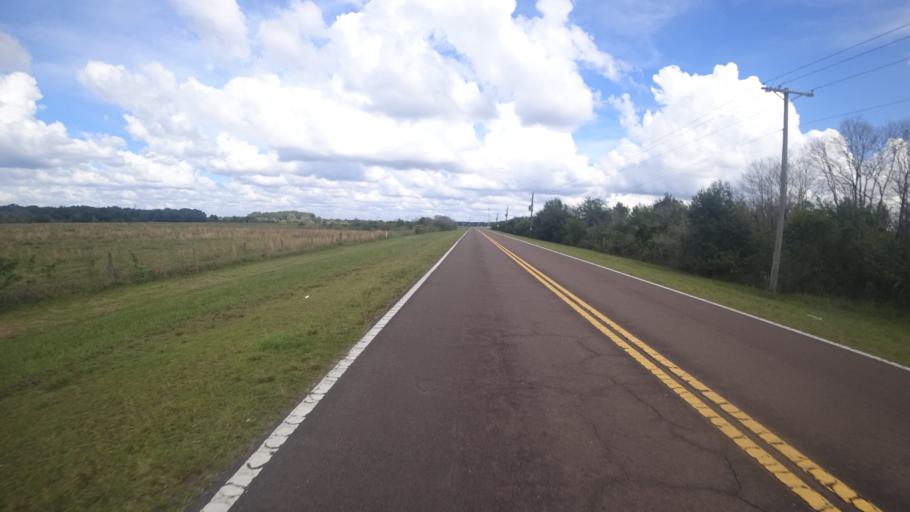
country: US
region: Florida
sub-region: Hillsborough County
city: Ruskin
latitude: 27.6554
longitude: -82.4472
